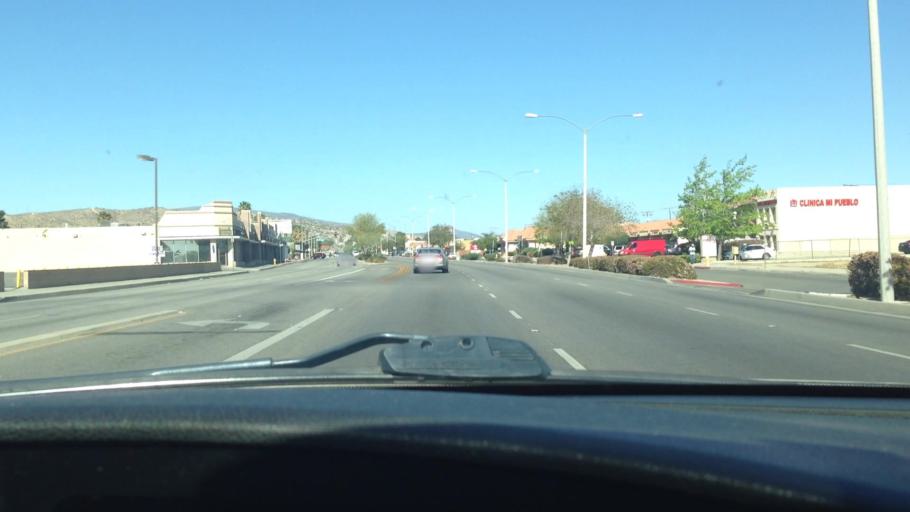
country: US
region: California
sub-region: Los Angeles County
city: Palmdale
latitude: 34.5798
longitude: -118.1218
